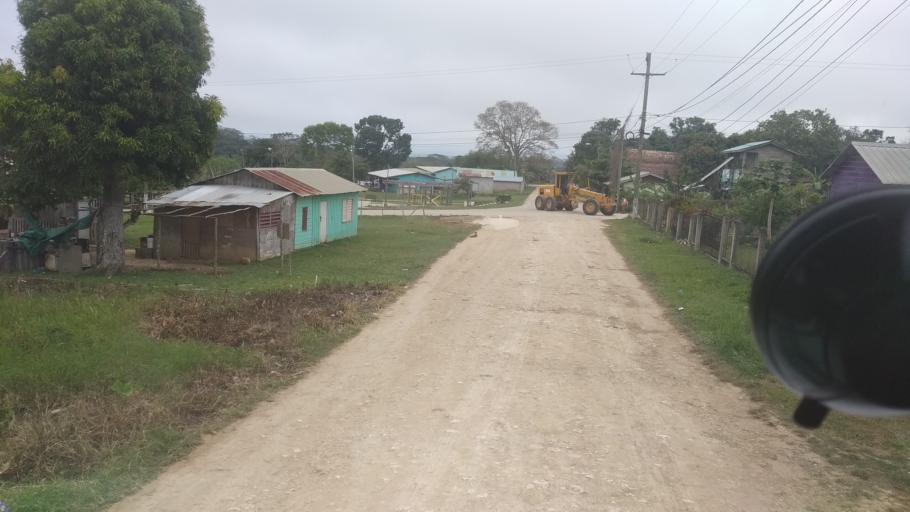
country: BZ
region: Cayo
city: Benque Viejo del Carmen
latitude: 17.0828
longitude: -89.1267
